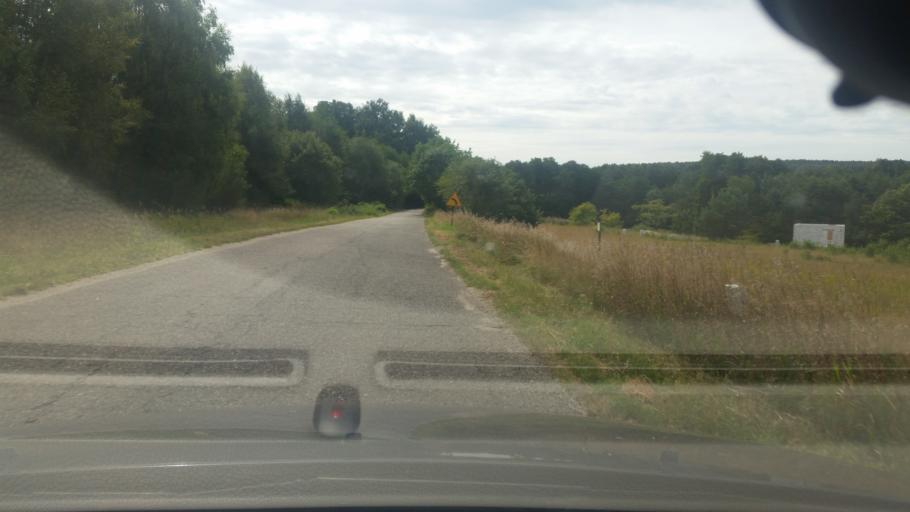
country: PL
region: Pomeranian Voivodeship
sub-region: Powiat wejherowski
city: Choczewo
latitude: 54.7623
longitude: 17.7924
